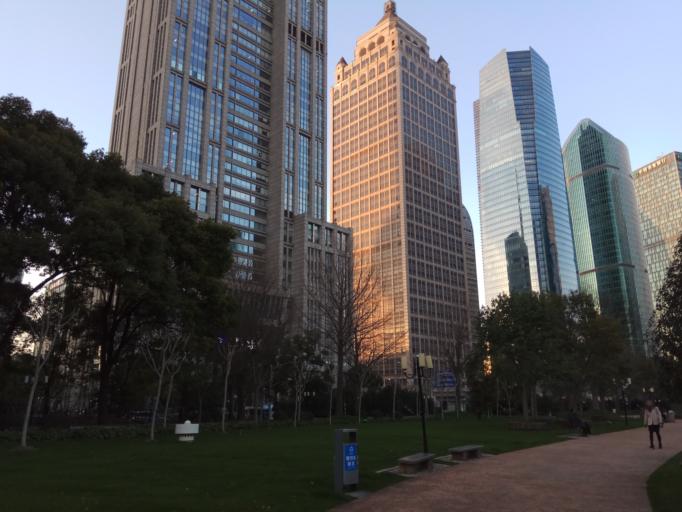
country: CN
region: Shanghai Shi
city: Hongkou
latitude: 31.2403
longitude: 121.5006
